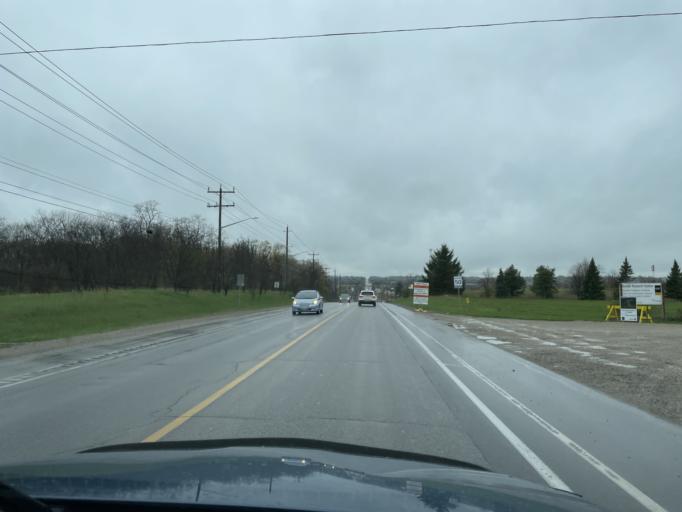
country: CA
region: Ontario
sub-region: Wellington County
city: Guelph
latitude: 43.5472
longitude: -80.2174
